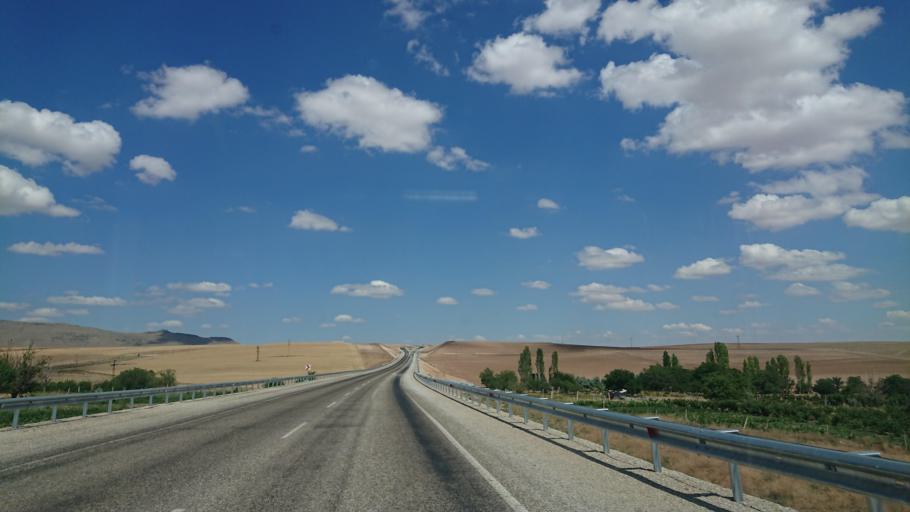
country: TR
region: Ankara
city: Evren
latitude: 39.1228
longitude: 33.9602
